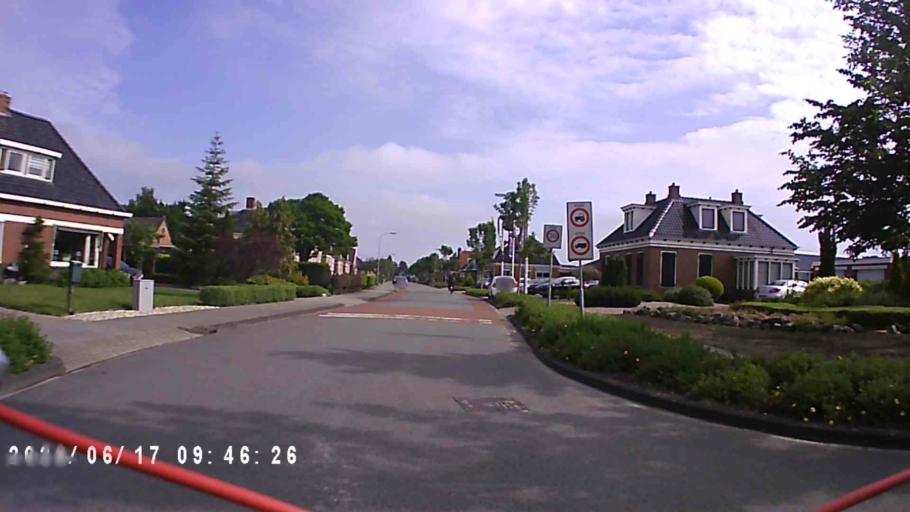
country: NL
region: Groningen
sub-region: Gemeente De Marne
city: Ulrum
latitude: 53.3554
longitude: 6.3378
